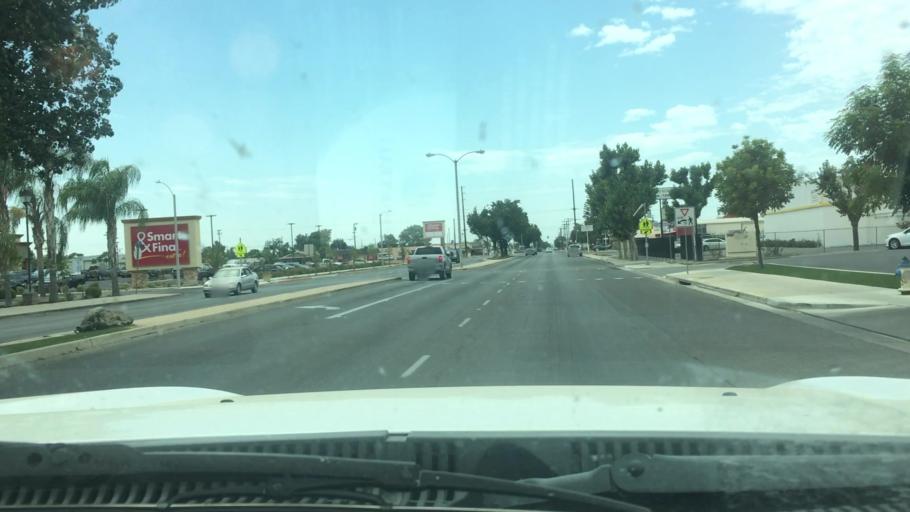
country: US
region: California
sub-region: Tulare County
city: Porterville
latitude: 36.0659
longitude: -119.0480
